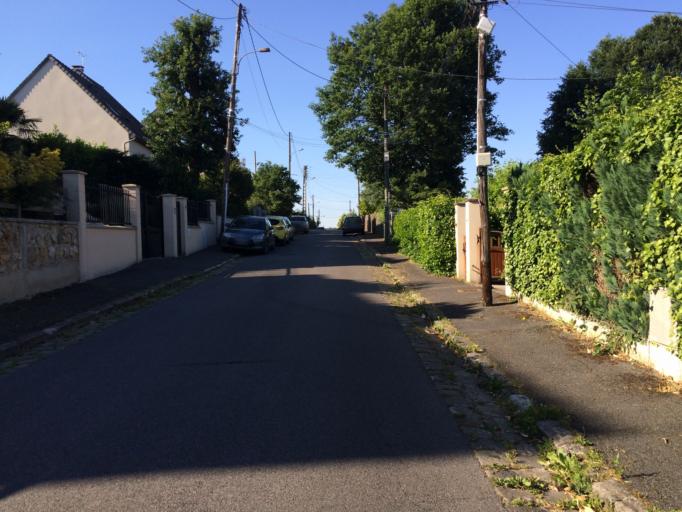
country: FR
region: Ile-de-France
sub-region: Departement de l'Essonne
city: Igny
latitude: 48.7273
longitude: 2.2239
